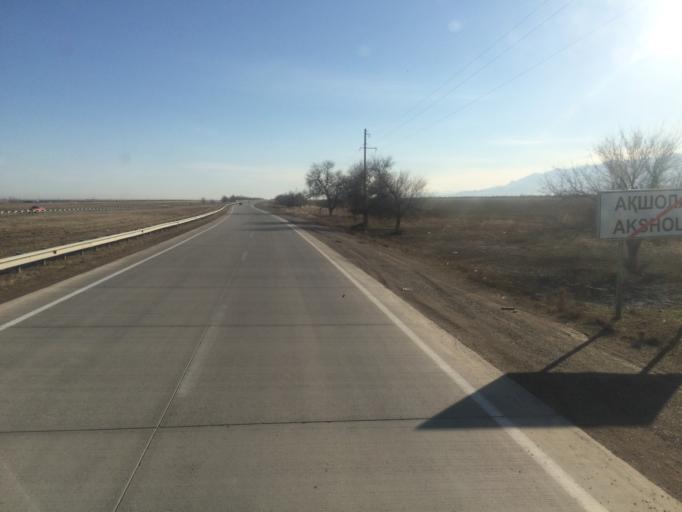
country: KZ
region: Zhambyl
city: Sarykemer
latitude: 43.0079
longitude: 71.8162
